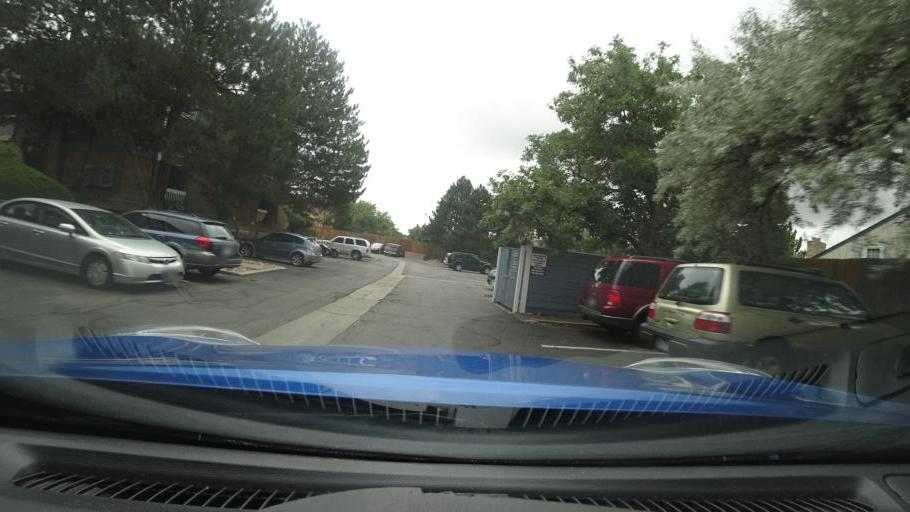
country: US
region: Colorado
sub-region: Adams County
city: Aurora
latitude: 39.6985
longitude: -104.8139
